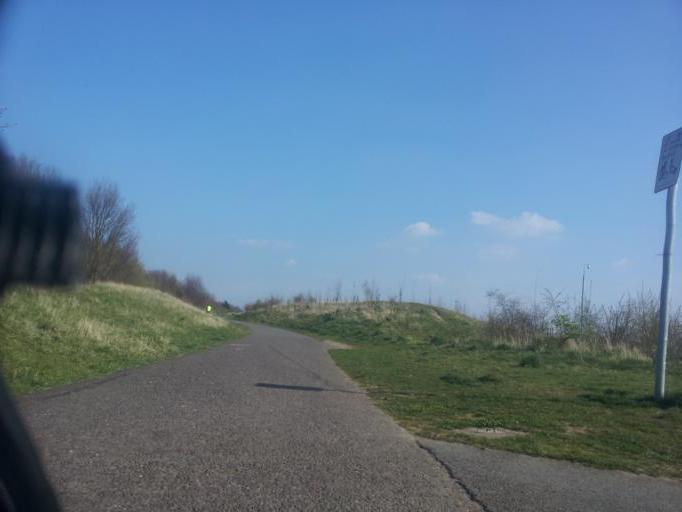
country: GB
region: England
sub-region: Kent
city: Gravesend
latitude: 51.4221
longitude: 0.3449
